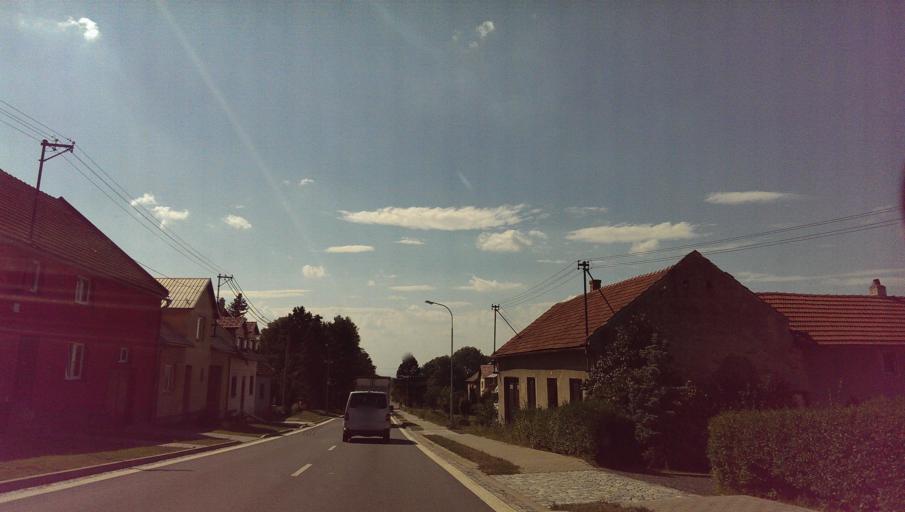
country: CZ
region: Zlin
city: Chvalcov
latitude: 49.4244
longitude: 17.7424
